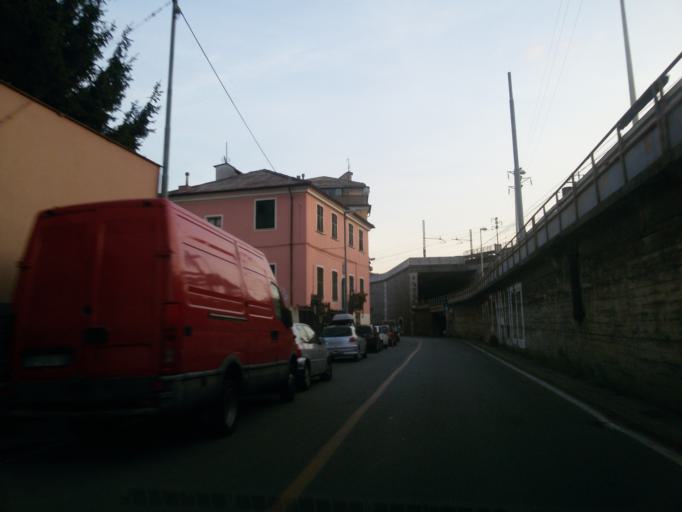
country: IT
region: Liguria
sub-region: Provincia di Genova
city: Genoa
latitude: 44.4391
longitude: 8.8912
